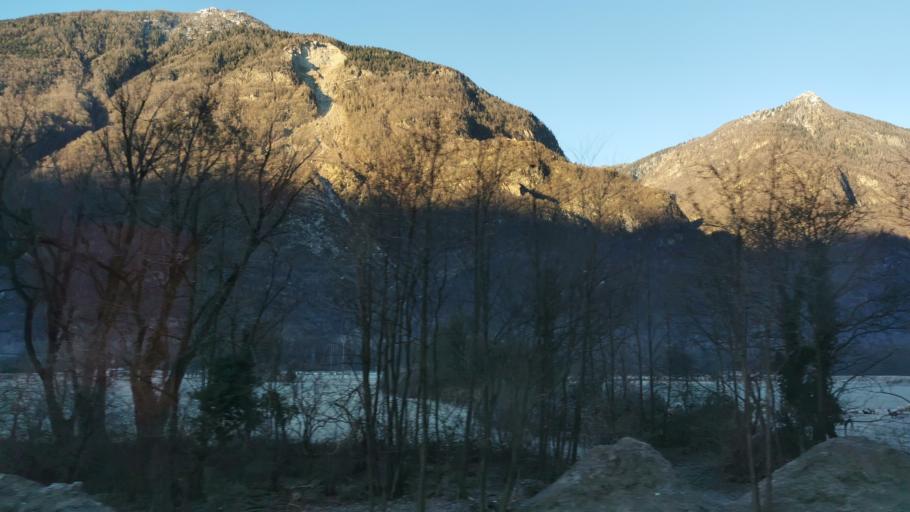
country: CH
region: Ticino
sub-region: Riviera District
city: Claro
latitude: 46.2574
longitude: 9.0164
